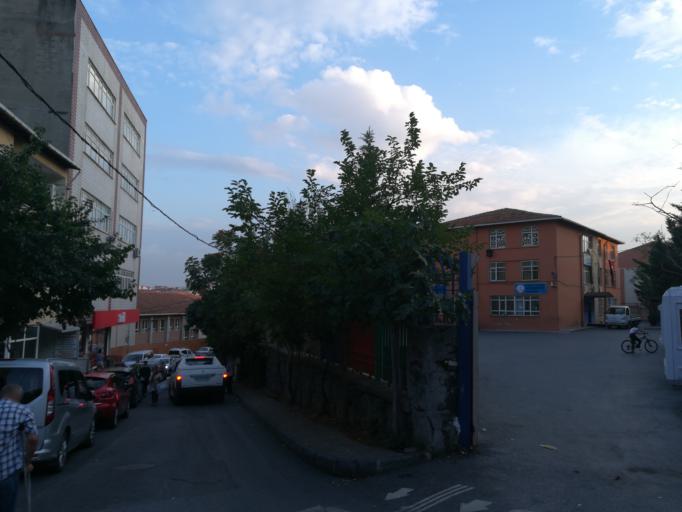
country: TR
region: Istanbul
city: Sisli
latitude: 41.0986
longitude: 28.9917
